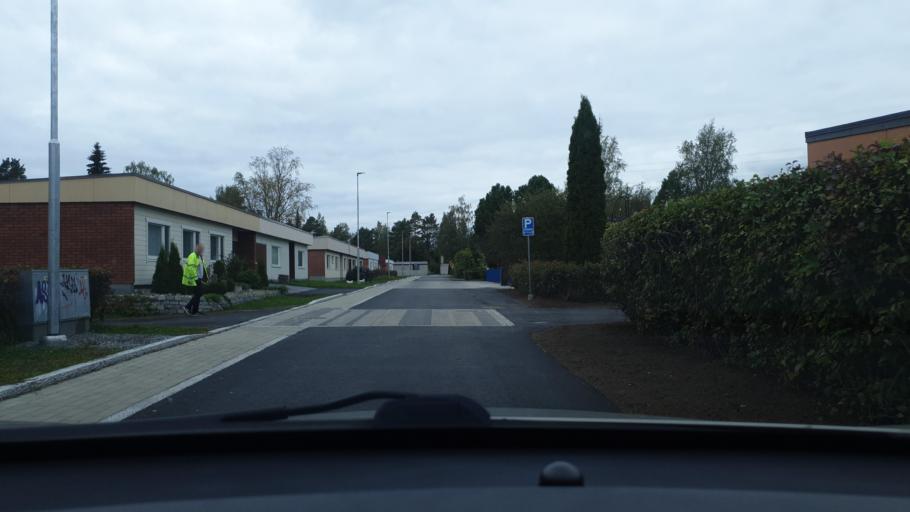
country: FI
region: Ostrobothnia
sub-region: Vaasa
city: Korsholm
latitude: 63.0957
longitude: 21.6717
